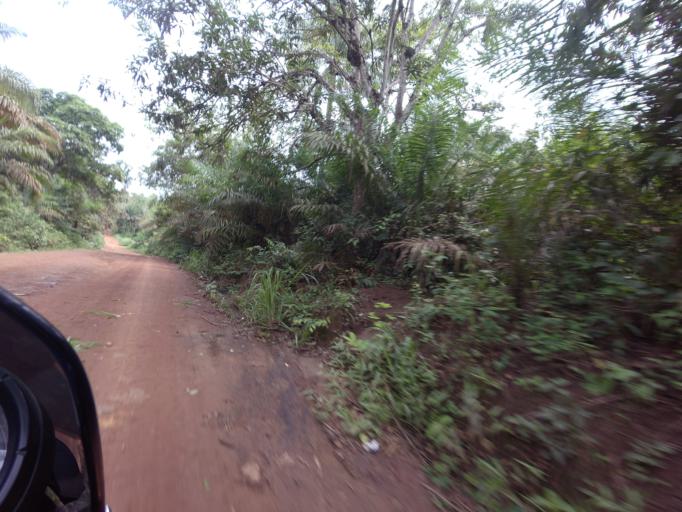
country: SL
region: Northern Province
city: Kambia
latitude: 9.1037
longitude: -12.9680
